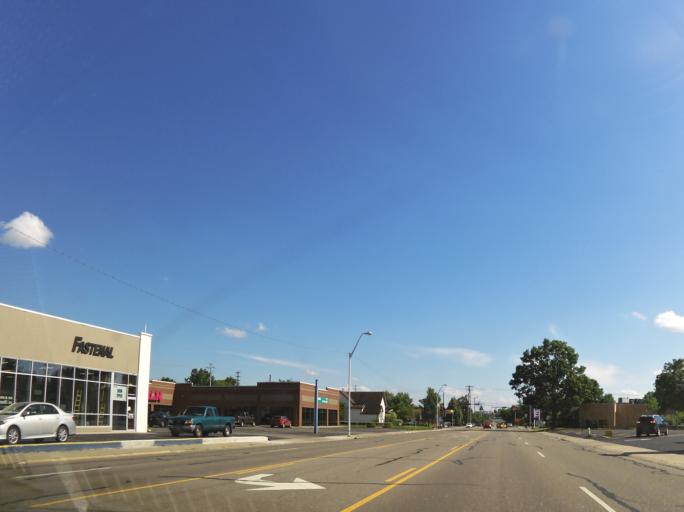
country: US
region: Ohio
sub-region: Greene County
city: Fairborn
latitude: 39.8206
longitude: -84.0212
